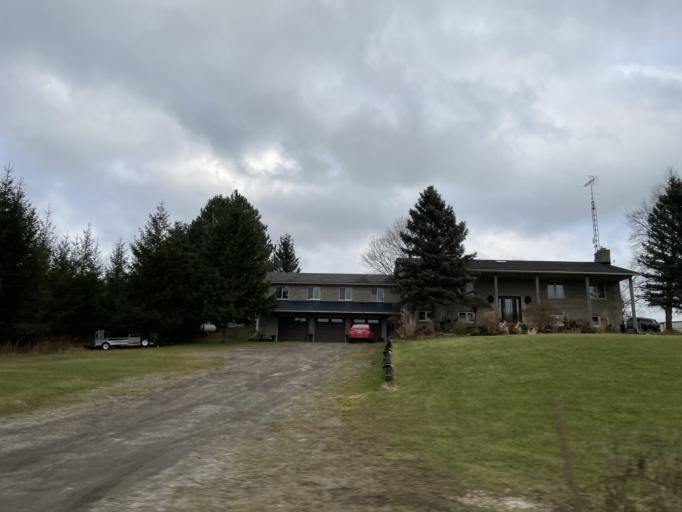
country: CA
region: Ontario
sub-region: Wellington County
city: Guelph
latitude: 43.4938
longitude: -80.3440
